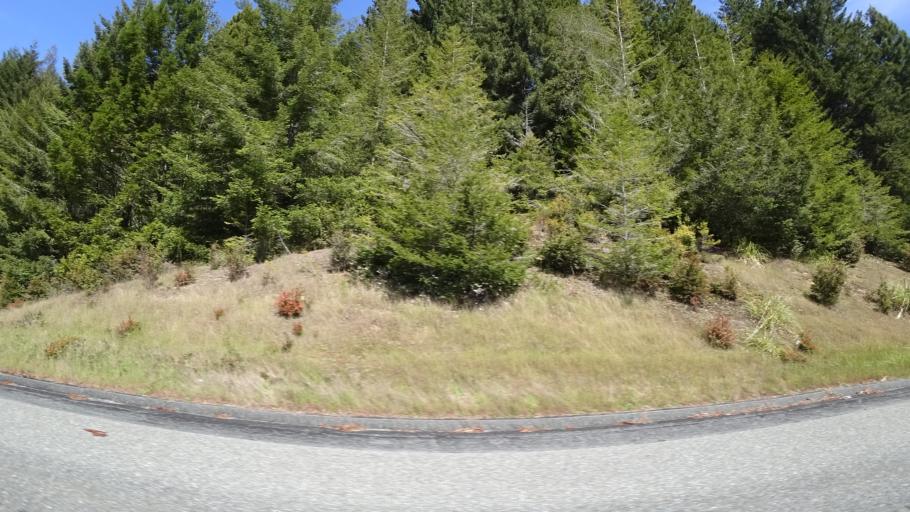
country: US
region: California
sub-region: Humboldt County
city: Westhaven-Moonstone
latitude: 41.3532
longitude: -124.0192
